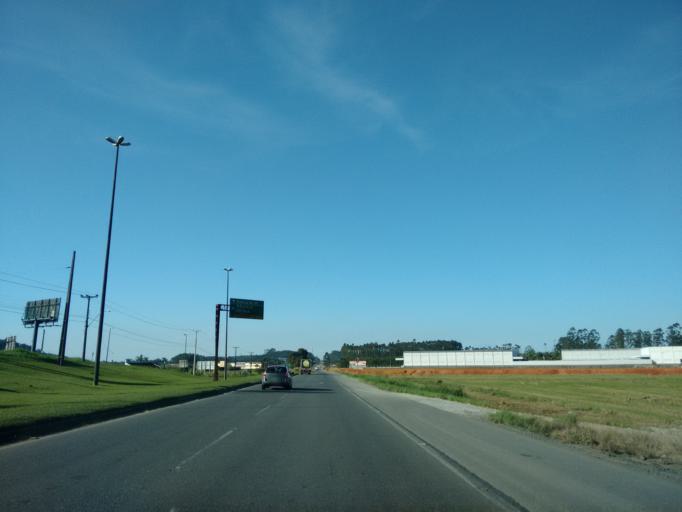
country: BR
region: Santa Catarina
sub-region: Guaramirim
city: Guaramirim
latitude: -26.4676
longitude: -48.9613
